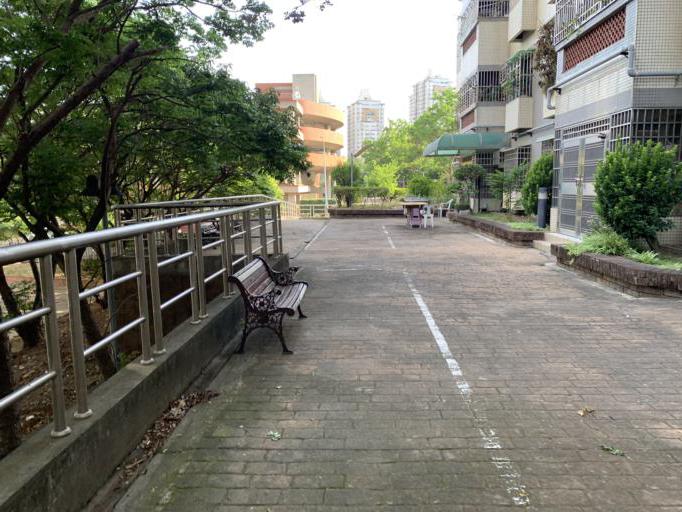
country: TW
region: Taiwan
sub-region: Taichung City
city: Taichung
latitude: 24.1920
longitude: 120.6094
